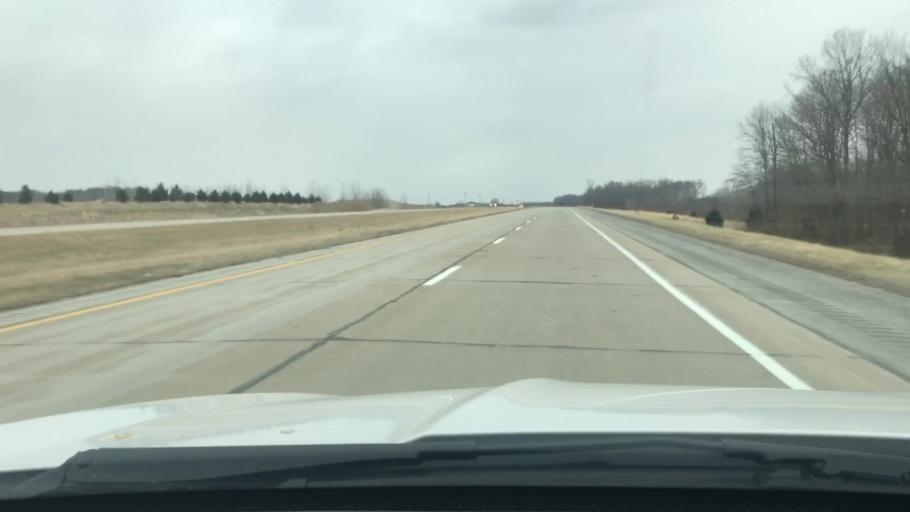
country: US
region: Indiana
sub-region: Cass County
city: Logansport
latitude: 40.7366
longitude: -86.2910
